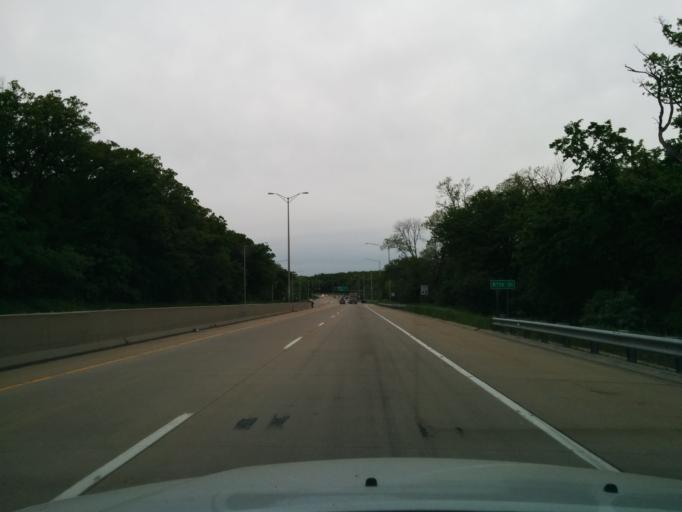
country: US
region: Illinois
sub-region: Cook County
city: Willow Springs
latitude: 41.7297
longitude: -87.8522
